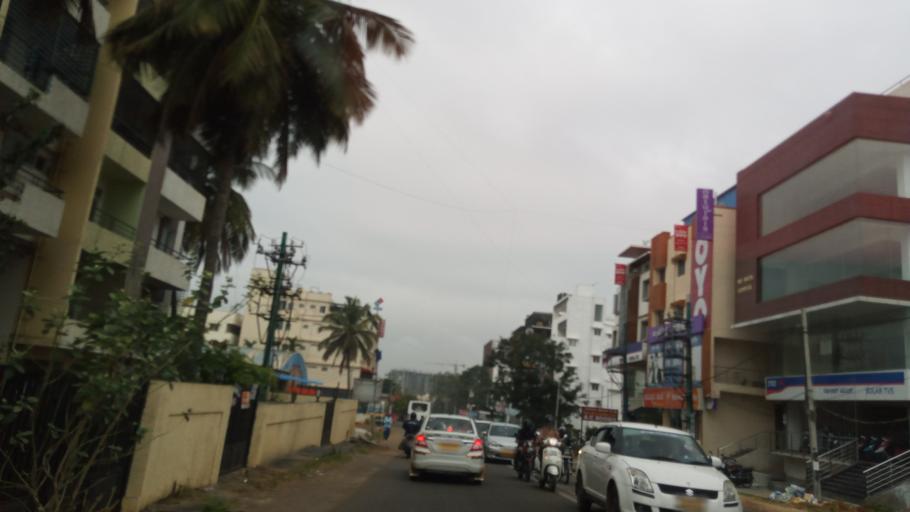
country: IN
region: Karnataka
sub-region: Bangalore Urban
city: Bangalore
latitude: 12.9036
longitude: 77.5151
